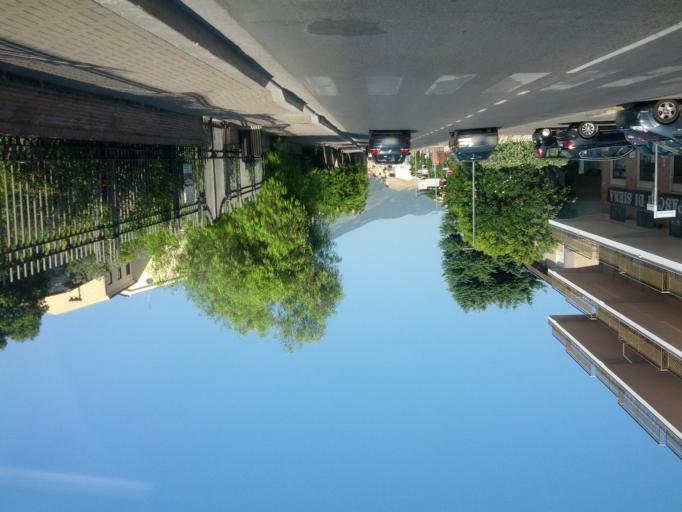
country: IT
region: Latium
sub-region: Provincia di Latina
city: Fondi
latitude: 41.3565
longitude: 13.4272
